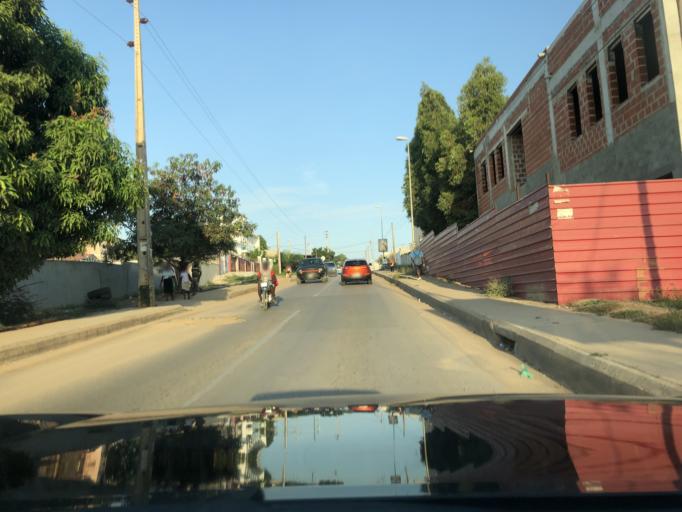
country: AO
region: Luanda
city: Luanda
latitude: -8.9447
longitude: 13.1590
